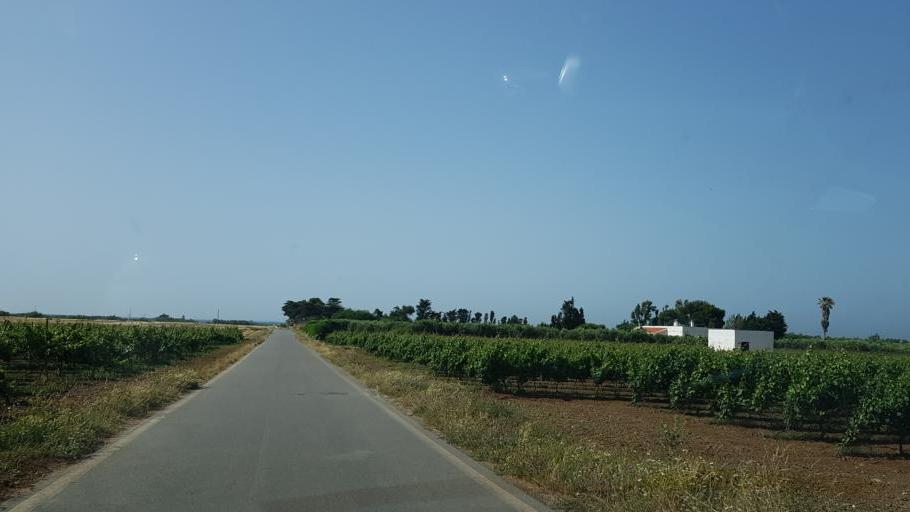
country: IT
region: Apulia
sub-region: Provincia di Brindisi
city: Brindisi
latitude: 40.6770
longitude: 17.8874
